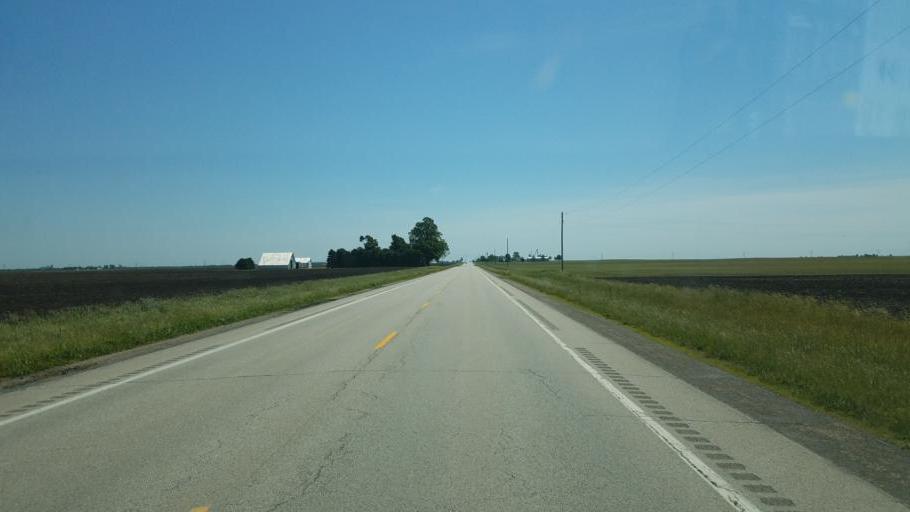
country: US
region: Illinois
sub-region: McLean County
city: Downs
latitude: 40.3120
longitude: -88.8587
